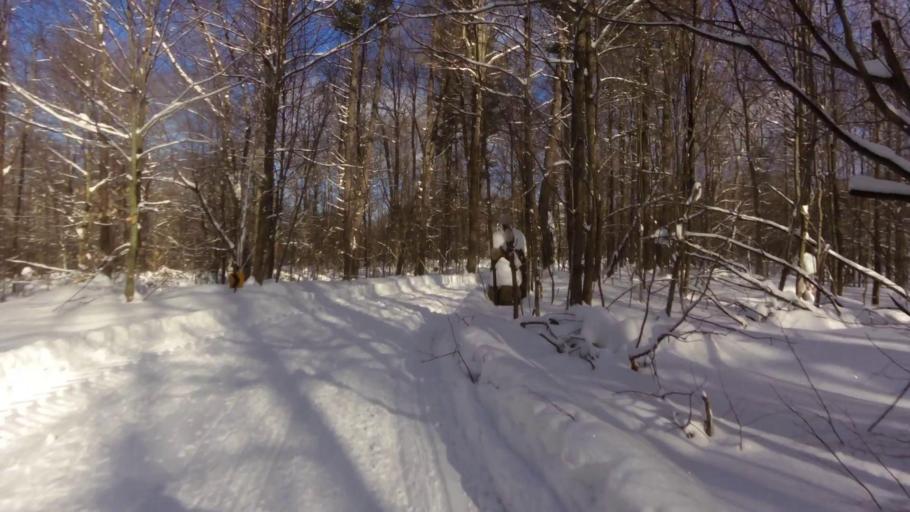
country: US
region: New York
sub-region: Chautauqua County
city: Falconer
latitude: 42.2598
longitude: -79.1451
